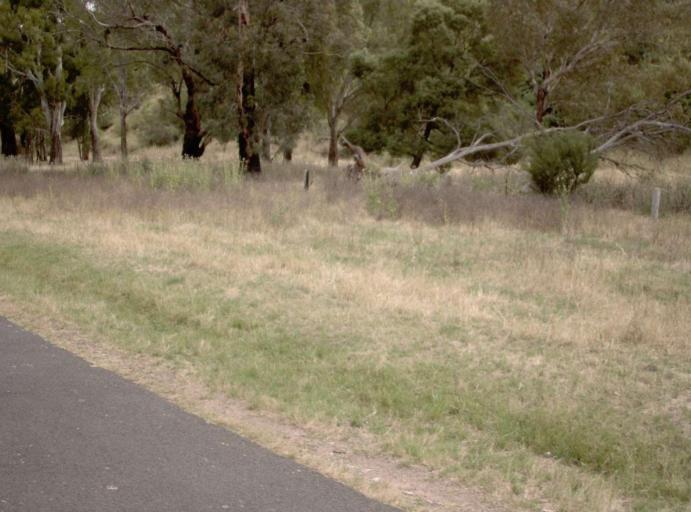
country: AU
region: Victoria
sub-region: Wellington
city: Heyfield
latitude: -37.6381
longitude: 146.6328
